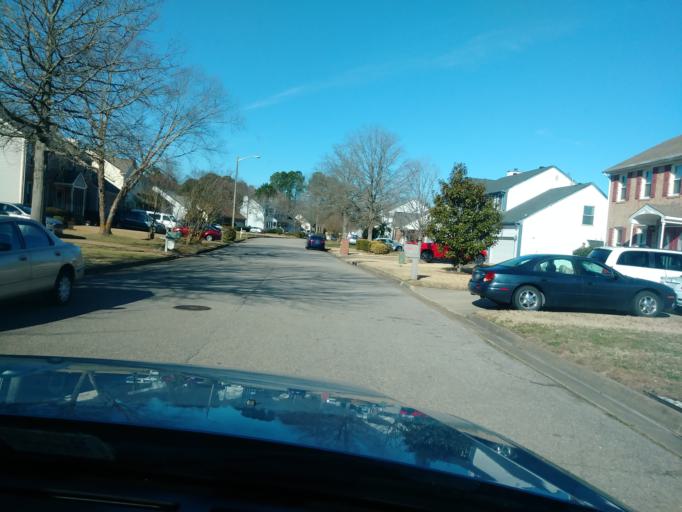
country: US
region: Virginia
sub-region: City of Chesapeake
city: Chesapeake
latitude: 36.7534
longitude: -76.2109
